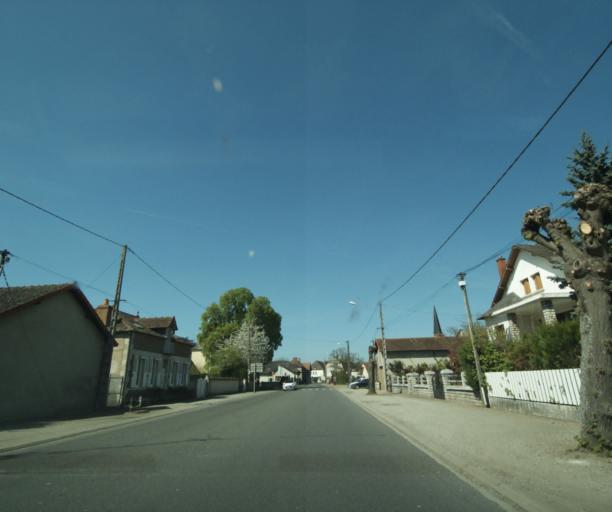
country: FR
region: Auvergne
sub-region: Departement de l'Allier
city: Trevol
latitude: 46.6582
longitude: 3.2522
